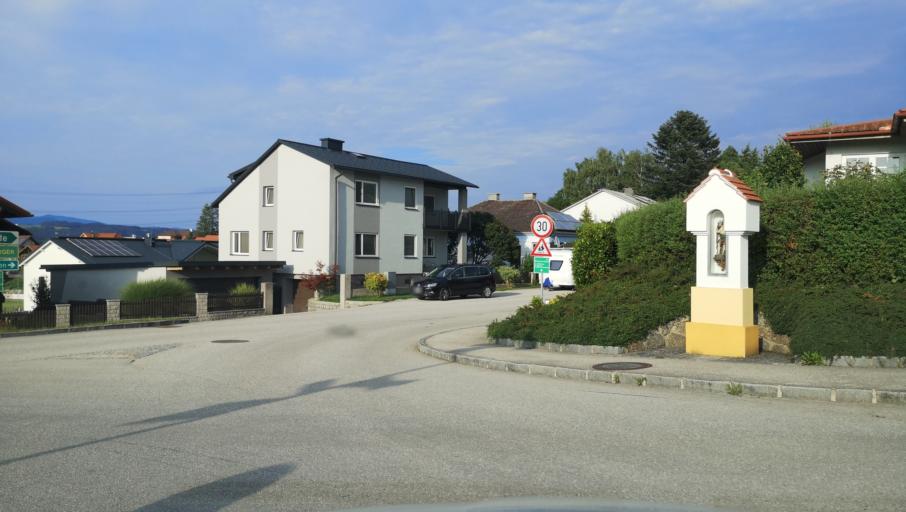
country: AT
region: Lower Austria
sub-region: Politischer Bezirk Amstetten
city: Amstetten
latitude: 48.1498
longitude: 14.8900
